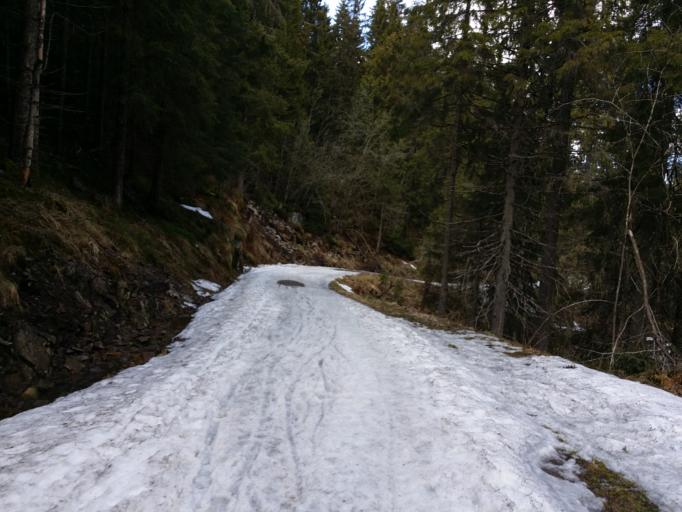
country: NO
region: Oslo
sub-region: Oslo
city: Sjolyststranda
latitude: 59.9856
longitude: 10.6884
